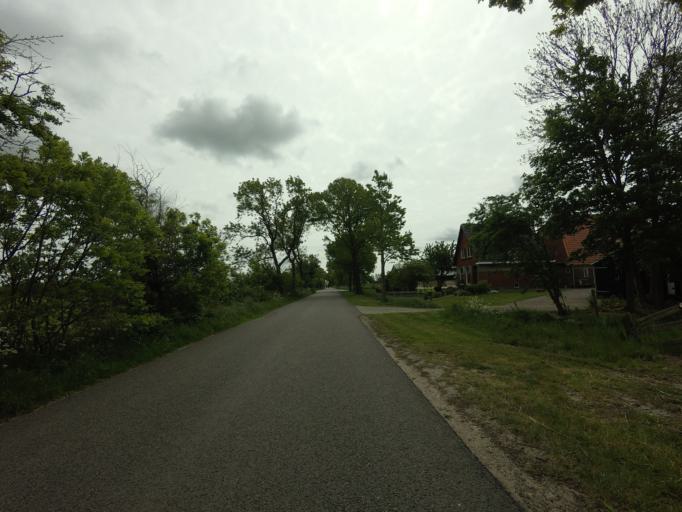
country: NL
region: Friesland
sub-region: Sudwest Fryslan
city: Koudum
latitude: 52.9060
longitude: 5.4618
